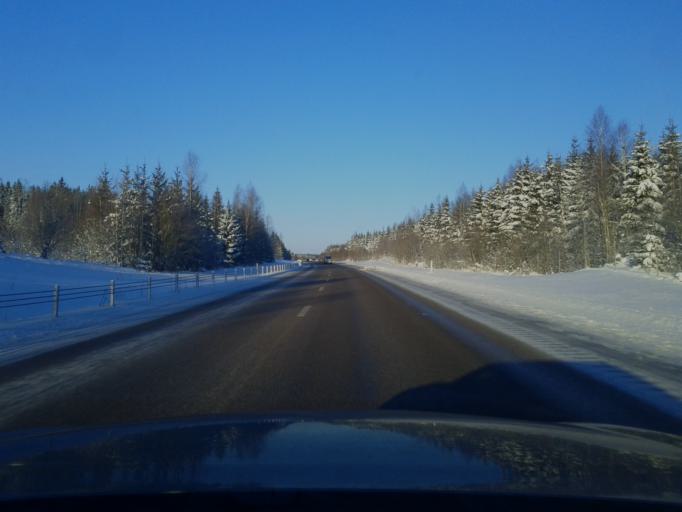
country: SE
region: Uppsala
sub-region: Tierps Kommun
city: Tierp
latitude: 60.3812
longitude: 17.4815
